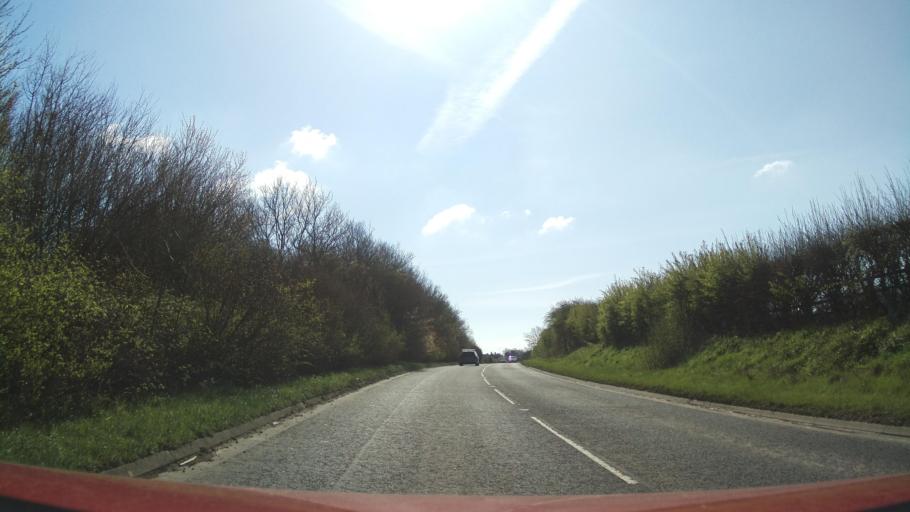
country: GB
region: England
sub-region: Wiltshire
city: Bradford-on-Avon
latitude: 51.3674
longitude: -2.2692
